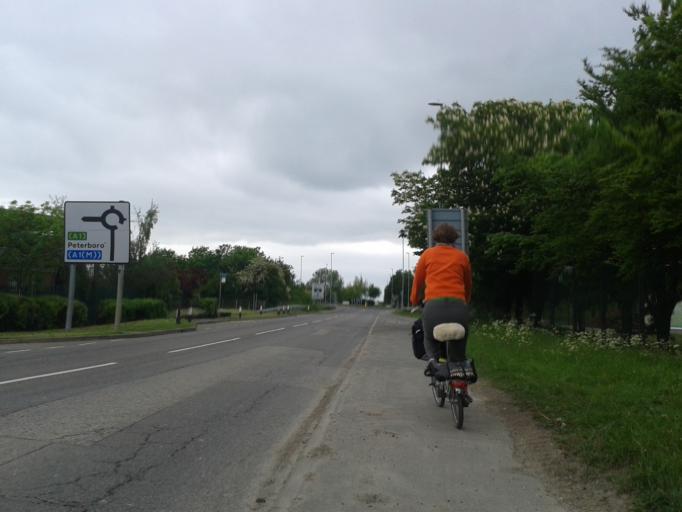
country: GB
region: England
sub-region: Cambridgeshire
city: Great Stukeley
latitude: 52.3722
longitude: -0.2415
